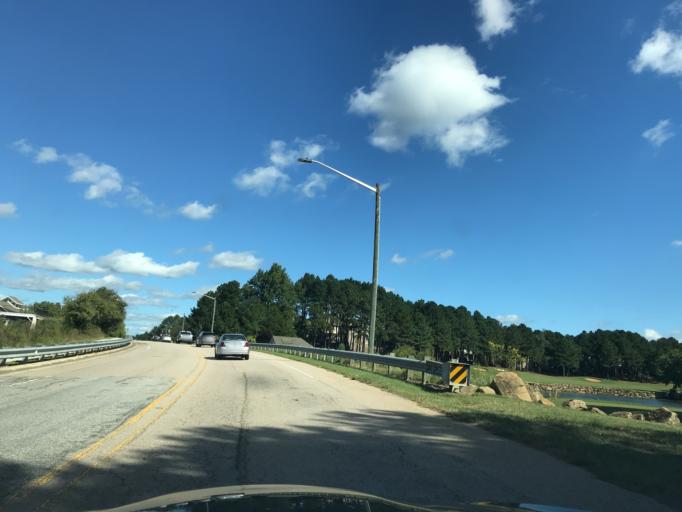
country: US
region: North Carolina
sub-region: Wake County
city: Wake Forest
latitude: 35.9493
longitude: -78.5010
